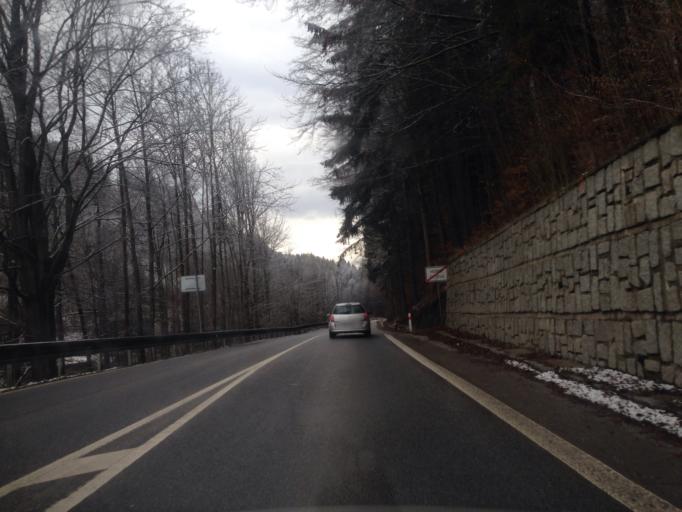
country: CZ
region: Liberecky
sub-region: Okres Semily
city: Ponikla
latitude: 50.6326
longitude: 15.4639
